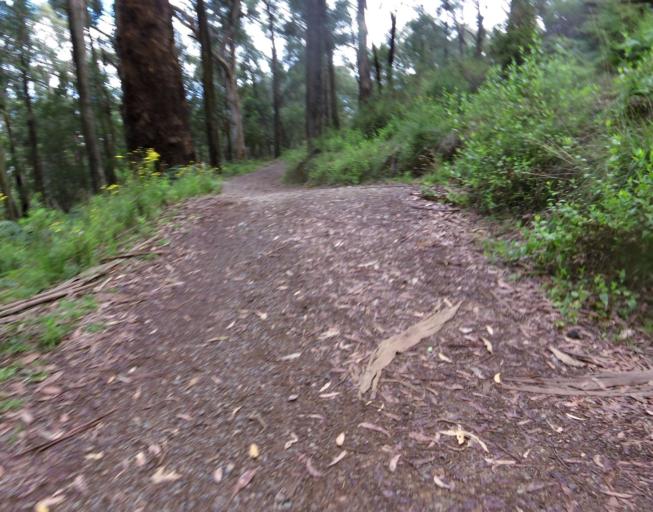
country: AU
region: Victoria
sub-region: Yarra Ranges
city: Montrose
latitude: -37.8377
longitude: 145.3430
